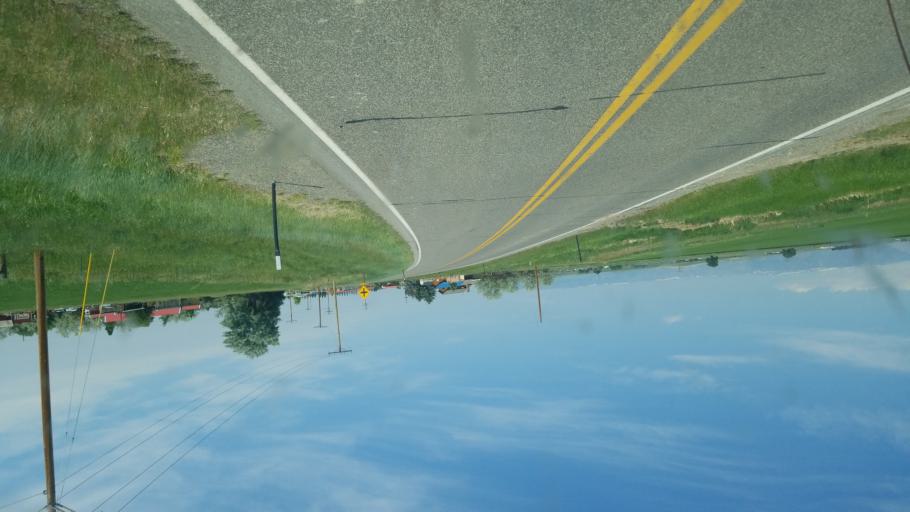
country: US
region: Wyoming
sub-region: Park County
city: Powell
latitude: 44.7229
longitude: -108.9318
